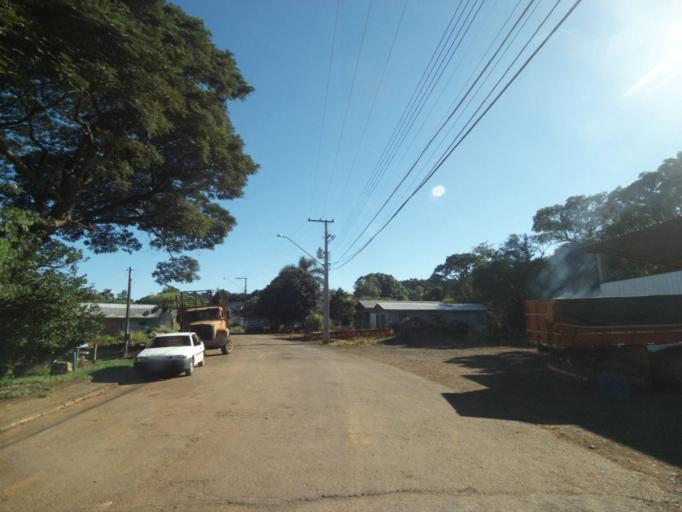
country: BR
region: Parana
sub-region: Pinhao
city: Pinhao
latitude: -25.8381
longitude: -52.0261
